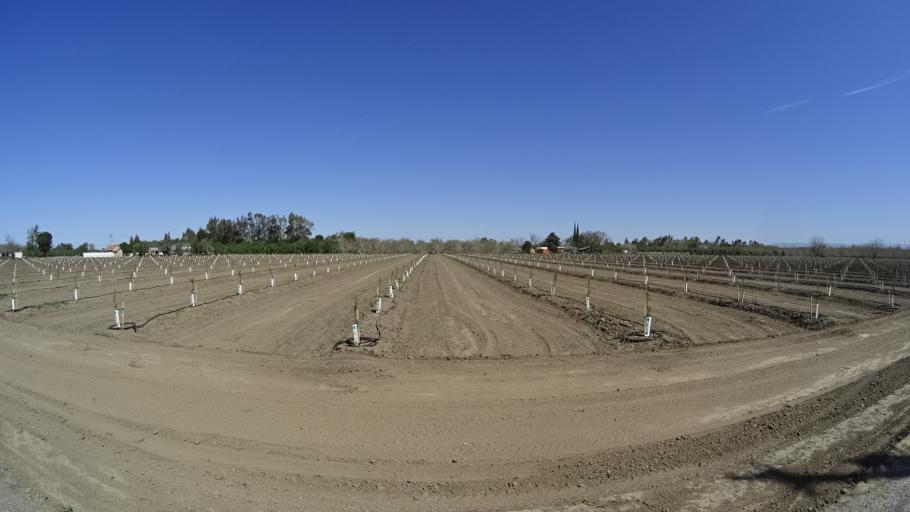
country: US
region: California
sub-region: Glenn County
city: Orland
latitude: 39.7429
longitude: -122.1253
